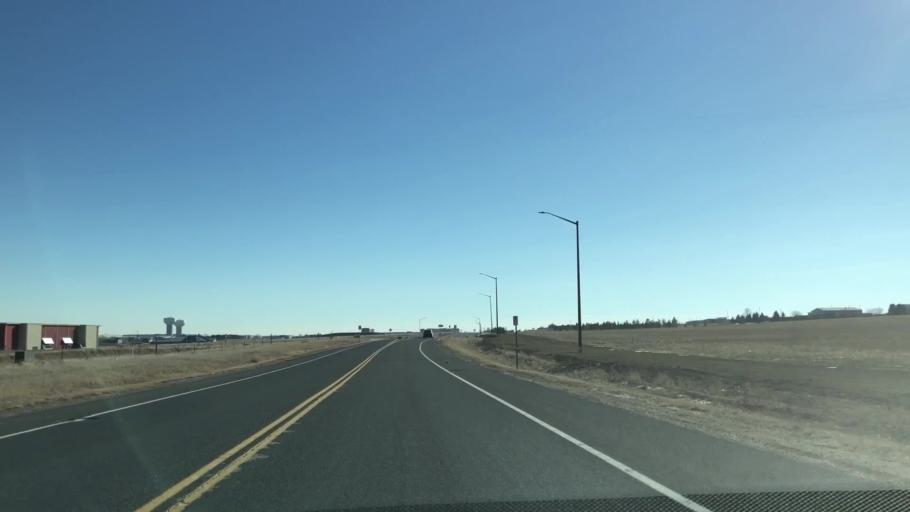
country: US
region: Colorado
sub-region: Weld County
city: Windsor
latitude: 40.4535
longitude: -104.9825
